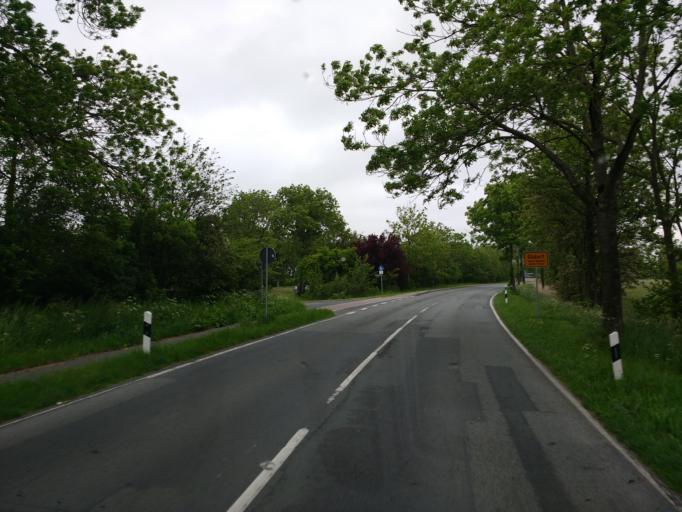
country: DE
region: Lower Saxony
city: Jever
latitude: 53.6329
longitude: 7.9224
